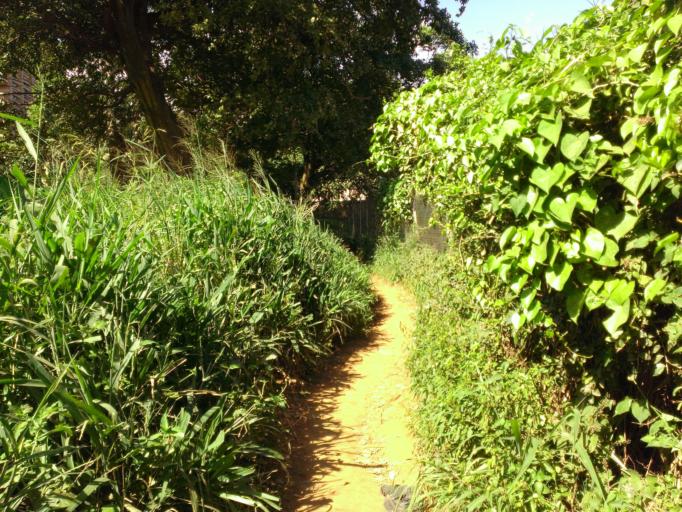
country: UG
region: Central Region
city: Kampala Central Division
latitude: 0.3301
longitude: 32.5656
